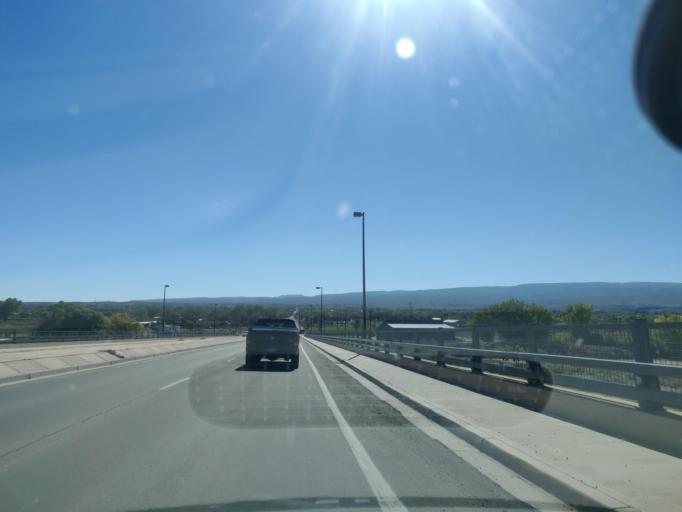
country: US
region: Colorado
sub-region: Mesa County
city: Fruitvale
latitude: 39.0711
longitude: -108.5148
